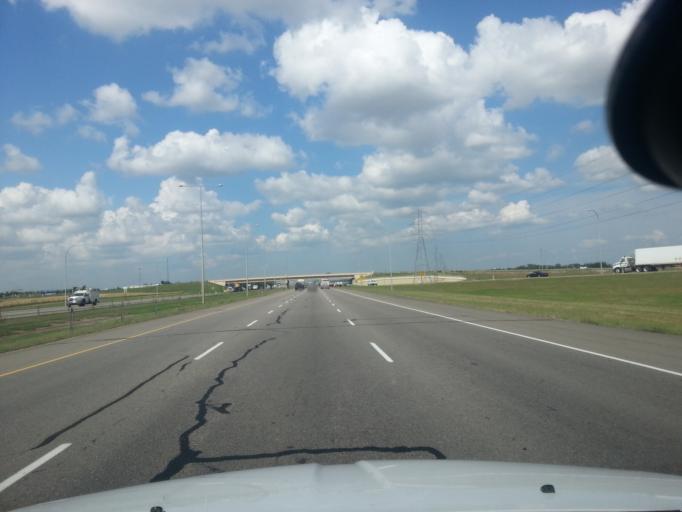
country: CA
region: Alberta
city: St. Albert
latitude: 53.5189
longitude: -113.6590
